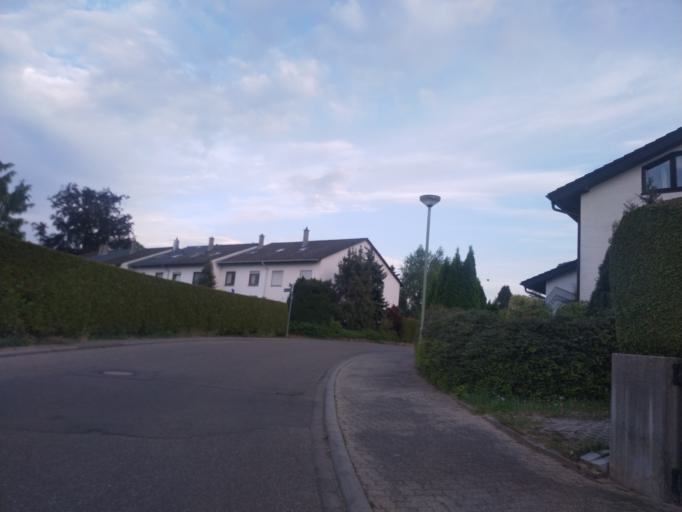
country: DE
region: Baden-Wuerttemberg
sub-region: Karlsruhe Region
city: Pforzheim
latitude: 48.8834
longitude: 8.6833
